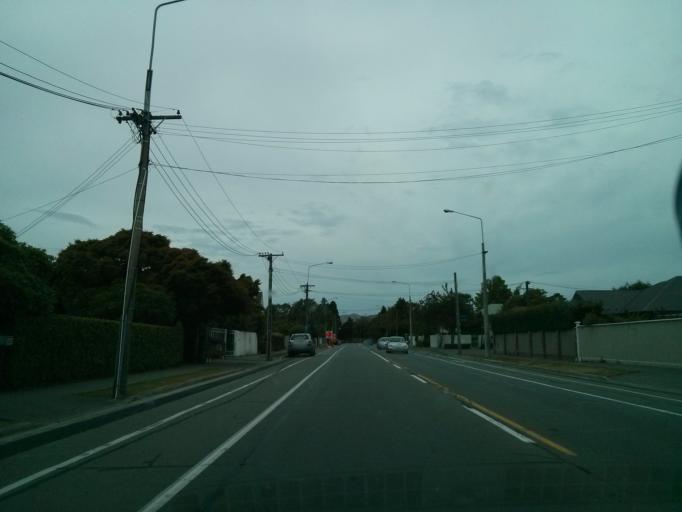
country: NZ
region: Canterbury
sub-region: Christchurch City
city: Christchurch
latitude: -43.5109
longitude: 172.6075
